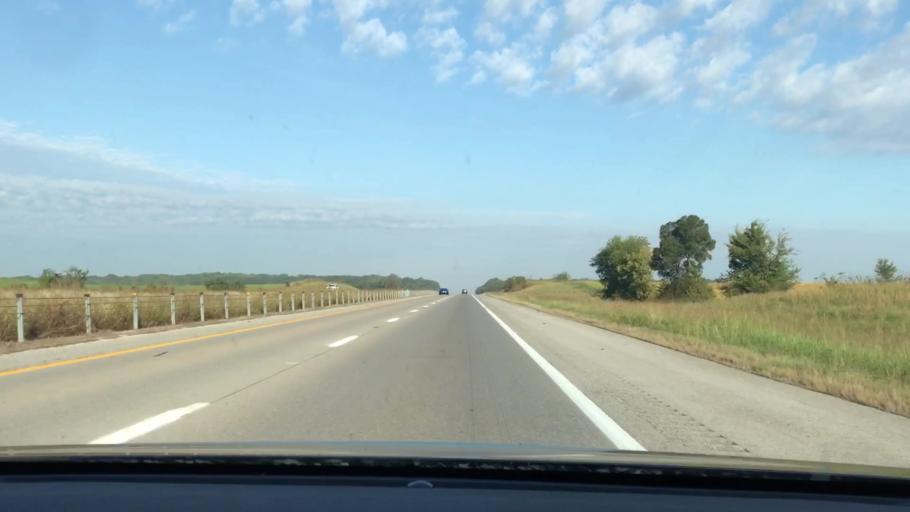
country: US
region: Kentucky
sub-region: Christian County
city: Hopkinsville
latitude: 36.7687
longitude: -87.5527
